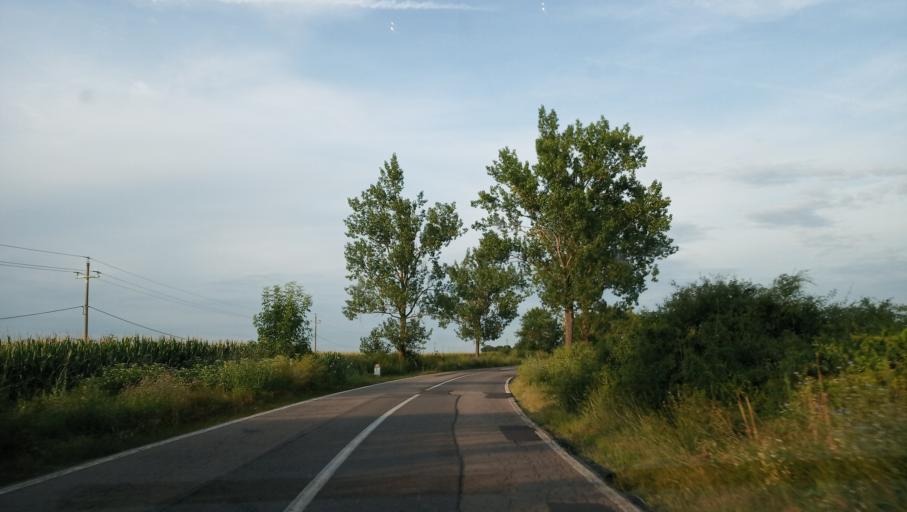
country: RO
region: Giurgiu
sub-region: Comuna Greaca
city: Greaca
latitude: 44.1159
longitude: 26.3605
